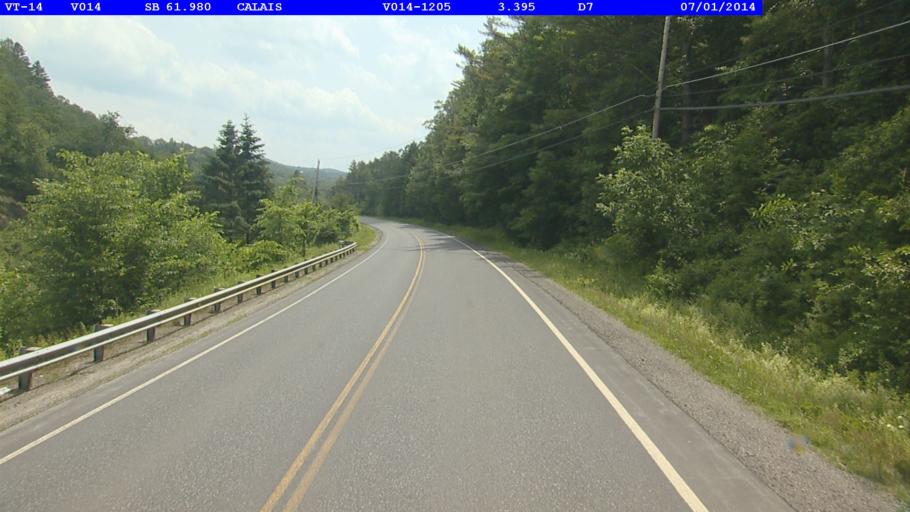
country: US
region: Vermont
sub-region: Washington County
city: Montpelier
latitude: 44.3546
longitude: -72.4450
